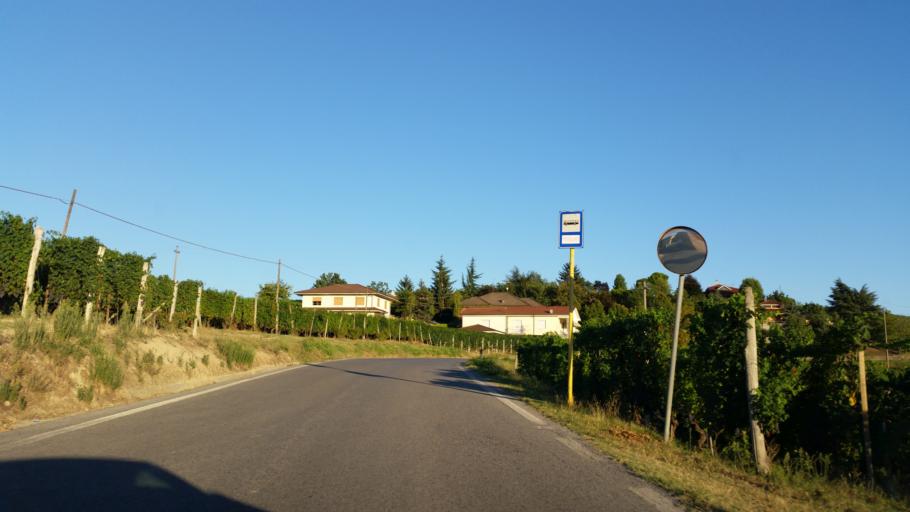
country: IT
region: Piedmont
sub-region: Provincia di Cuneo
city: Barbaresco
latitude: 44.7121
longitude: 8.0903
